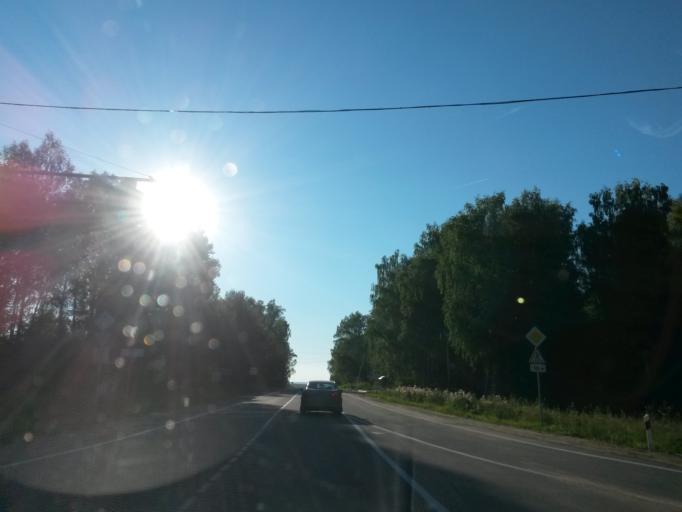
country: RU
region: Jaroslavl
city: Gavrilov-Yam
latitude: 57.2724
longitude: 39.9498
